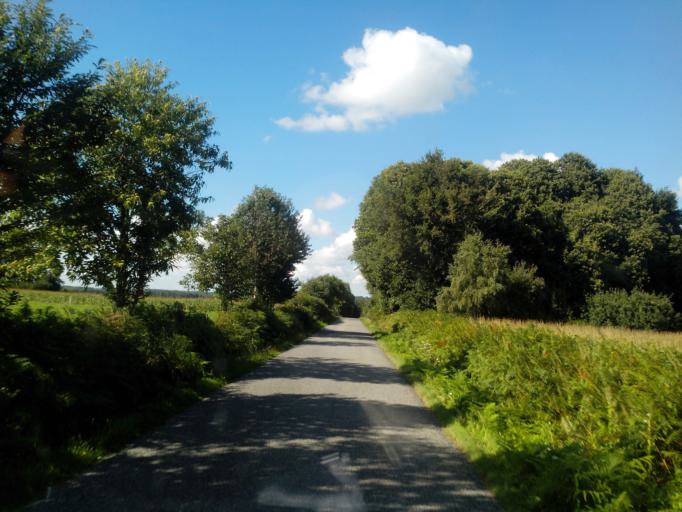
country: FR
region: Brittany
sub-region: Departement des Cotes-d'Armor
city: Merdrignac
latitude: 48.1661
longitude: -2.4182
